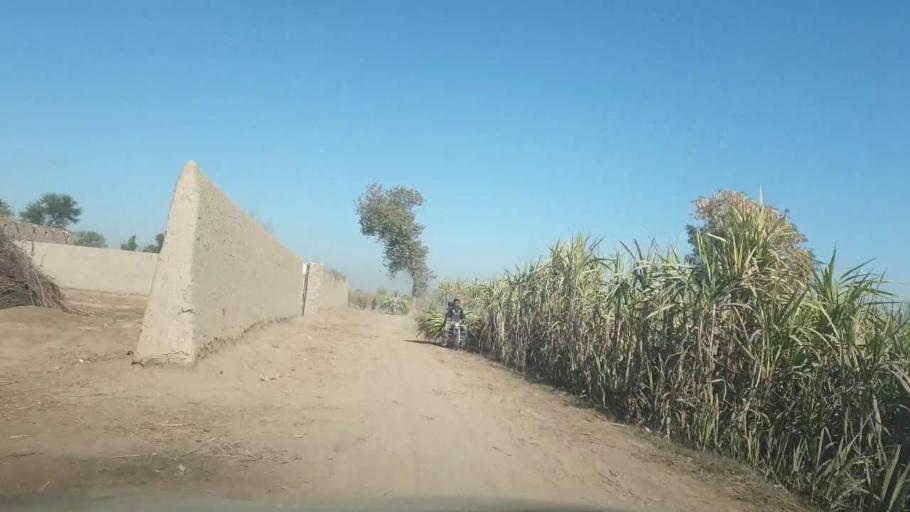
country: PK
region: Sindh
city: Ghotki
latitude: 27.9750
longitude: 69.3411
